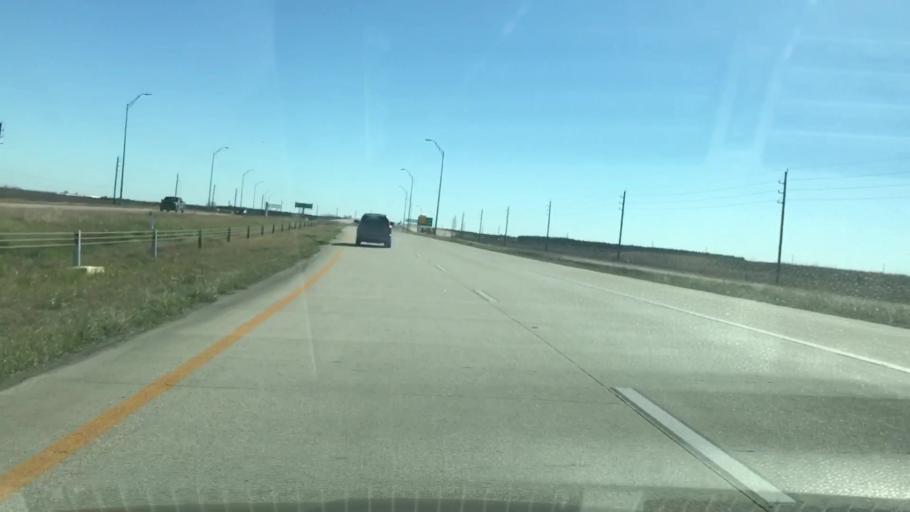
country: US
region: Texas
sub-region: Harris County
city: Cypress
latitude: 29.9113
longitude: -95.7616
